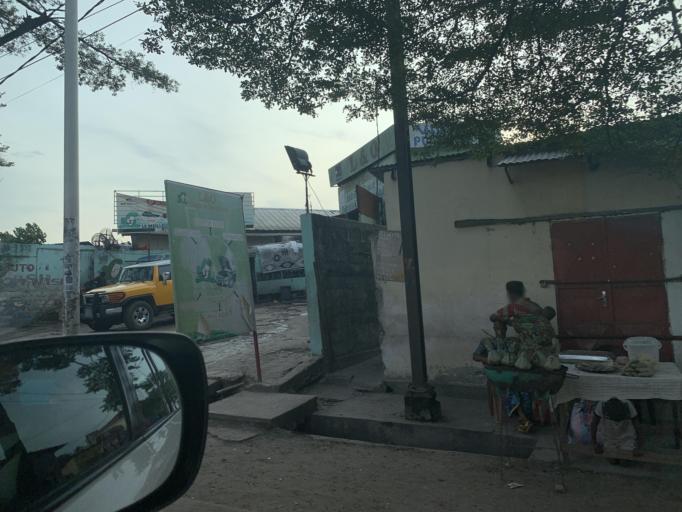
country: CG
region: Brazzaville
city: Brazzaville
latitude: -4.2611
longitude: 15.2897
